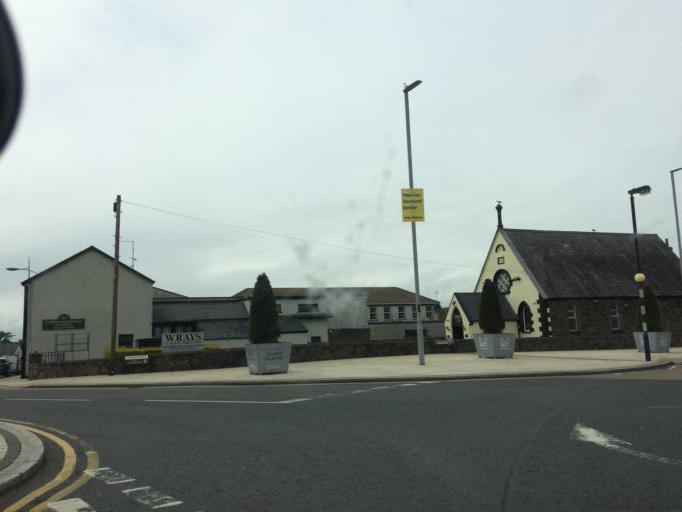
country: GB
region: Northern Ireland
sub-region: Antrim Borough
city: Antrim
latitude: 54.7139
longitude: -6.2151
